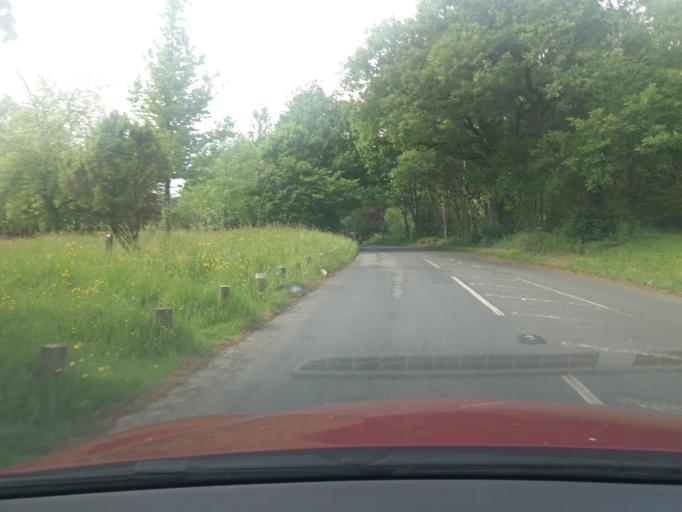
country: GB
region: England
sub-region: Borough of Bolton
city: Horwich
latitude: 53.6209
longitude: -2.5628
